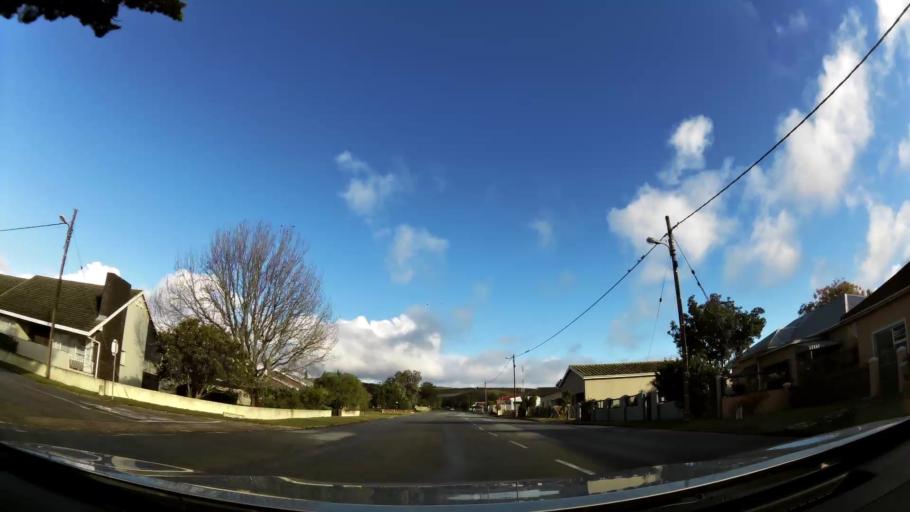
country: ZA
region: Western Cape
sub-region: Eden District Municipality
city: Riversdale
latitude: -34.2067
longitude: 21.5863
